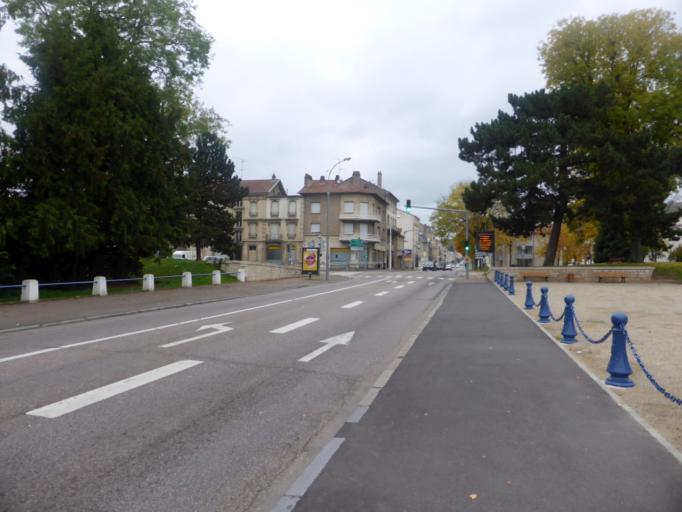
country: FR
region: Lorraine
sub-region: Departement de Meurthe-et-Moselle
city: Toul
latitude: 48.6748
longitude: 5.8855
